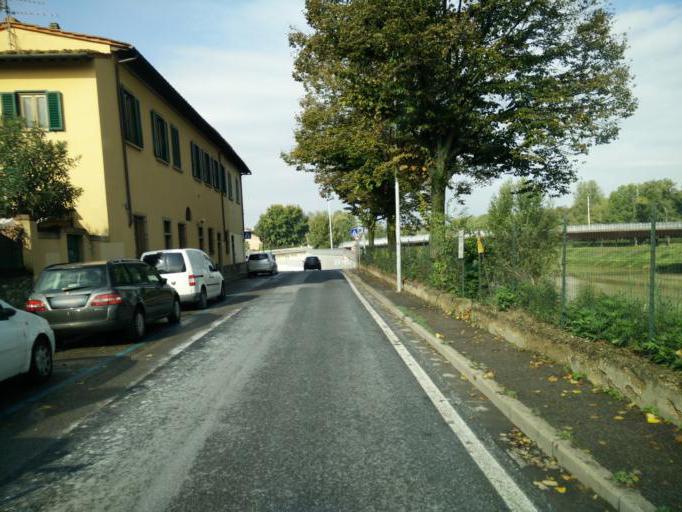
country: IT
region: Tuscany
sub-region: Province of Florence
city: Florence
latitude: 43.7753
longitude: 11.2306
